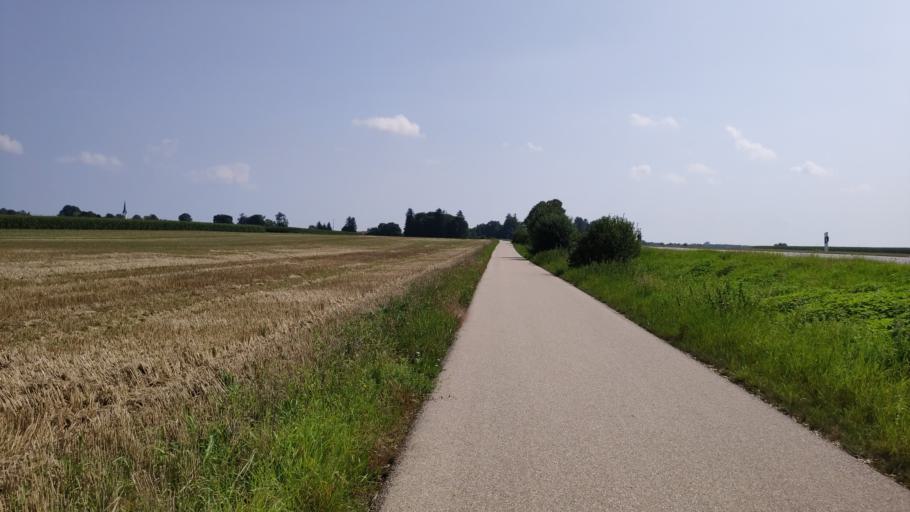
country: DE
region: Bavaria
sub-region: Swabia
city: Kleinaitingen
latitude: 48.2168
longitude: 10.8284
